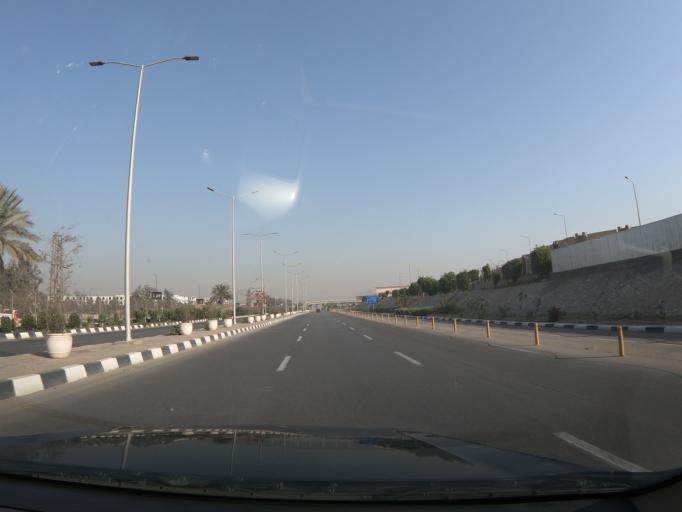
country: EG
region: Muhafazat al Qalyubiyah
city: Al Khankah
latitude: 30.1065
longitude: 31.3866
